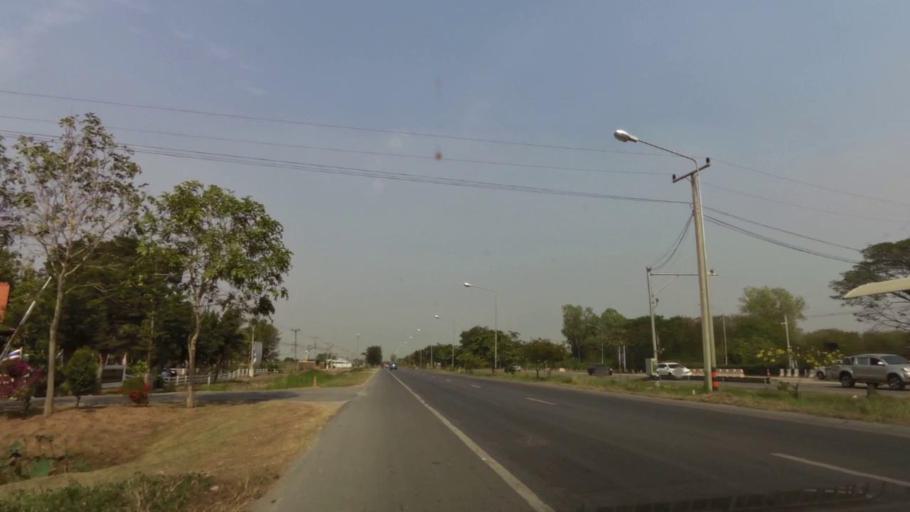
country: TH
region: Phra Nakhon Si Ayutthaya
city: Phra Nakhon Si Ayutthaya
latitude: 14.3119
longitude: 100.5278
